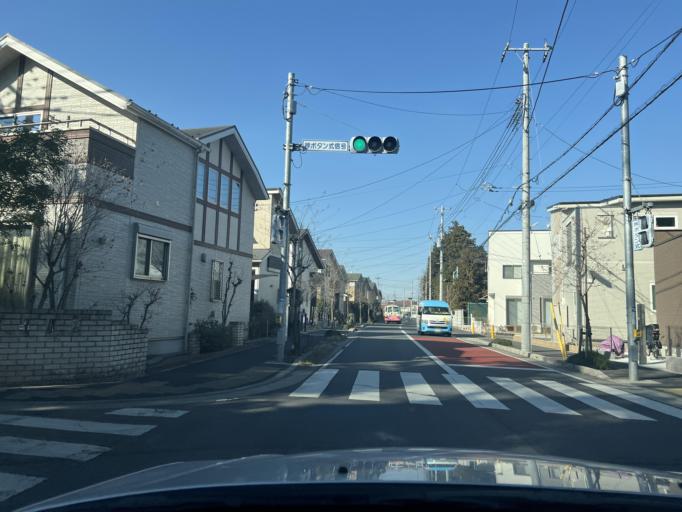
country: JP
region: Chiba
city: Nagareyama
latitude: 35.8911
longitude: 139.9110
